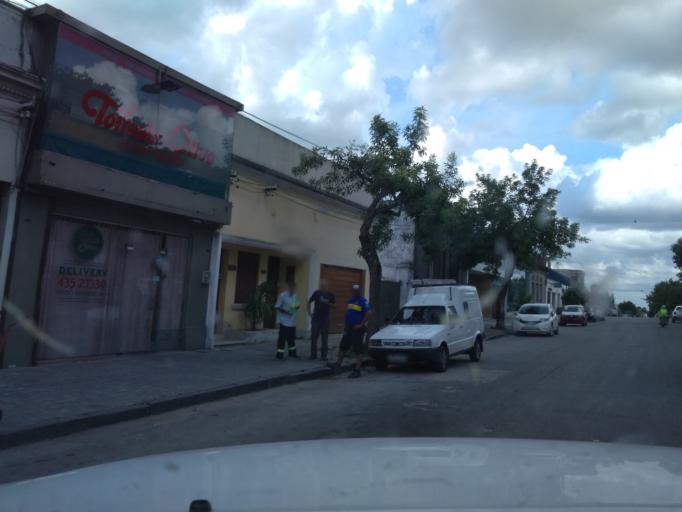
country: UY
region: Florida
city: Florida
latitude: -34.0938
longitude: -56.2194
